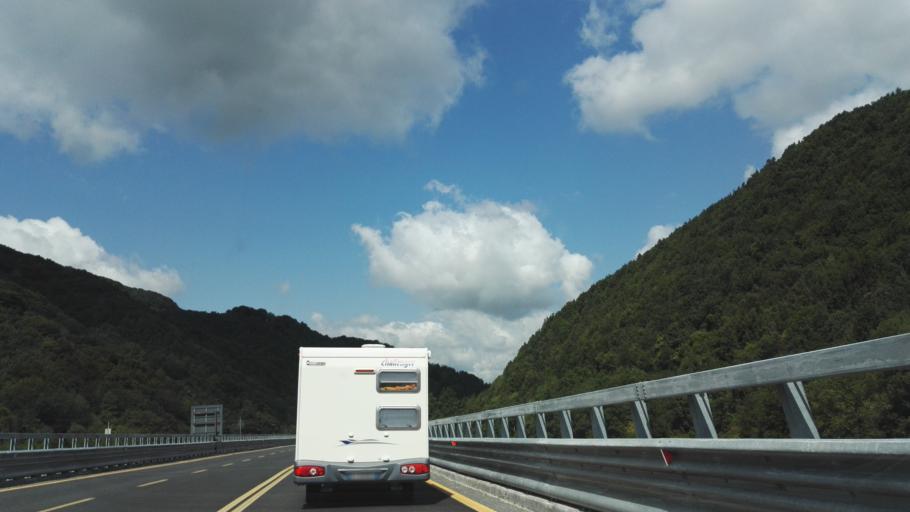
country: IT
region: Calabria
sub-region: Provincia di Reggio Calabria
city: Amato
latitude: 38.4049
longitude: 16.1541
